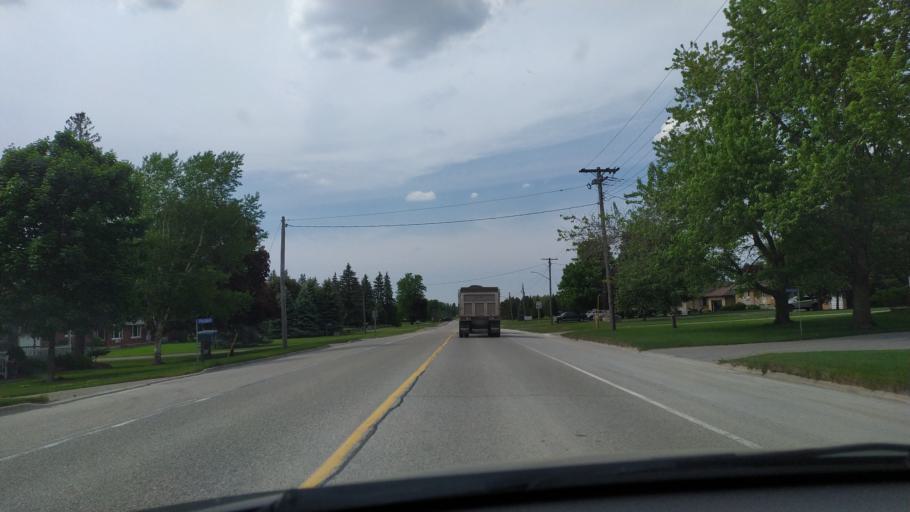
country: CA
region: Ontario
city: Stratford
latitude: 43.2181
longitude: -81.0700
